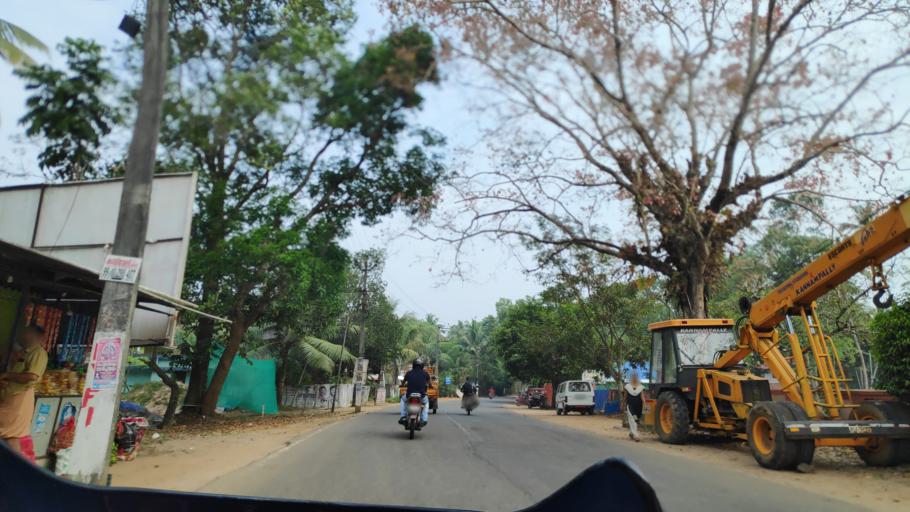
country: IN
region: Kerala
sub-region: Alappuzha
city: Vayalar
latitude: 9.7144
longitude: 76.3590
